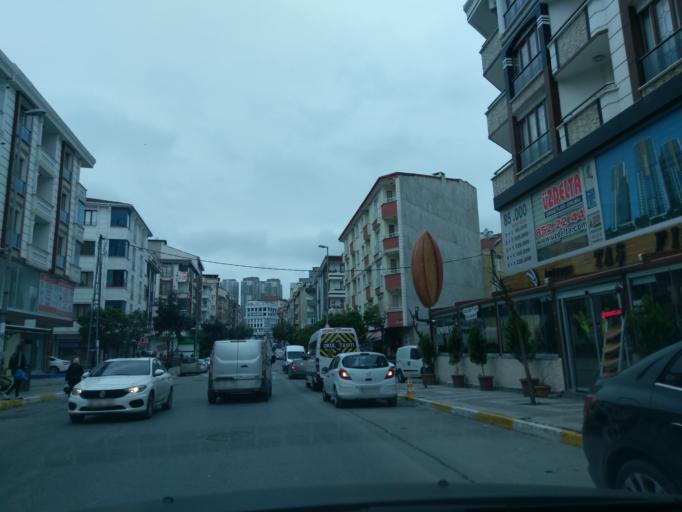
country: TR
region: Istanbul
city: Esenyurt
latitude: 41.0157
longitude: 28.6638
